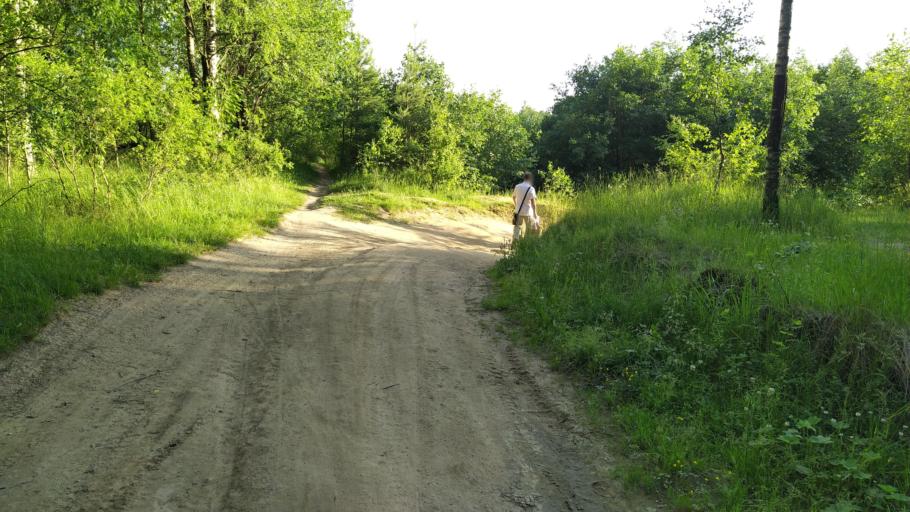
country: RU
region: Leningrad
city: Toksovo
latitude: 60.1107
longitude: 30.5312
